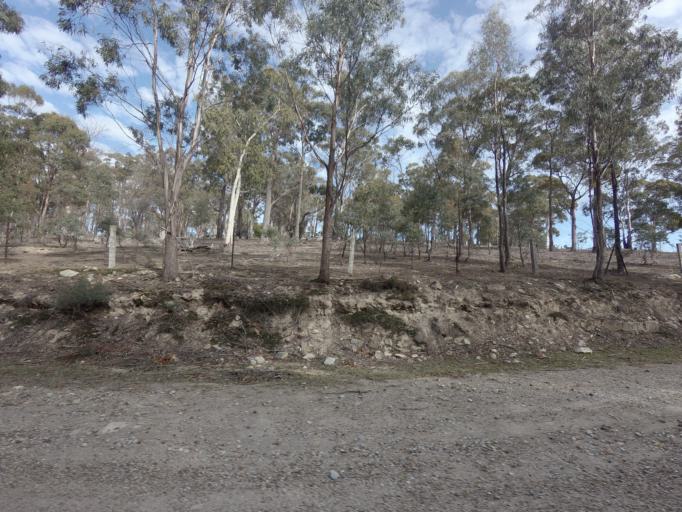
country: AU
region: Tasmania
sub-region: Sorell
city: Sorell
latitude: -42.5658
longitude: 147.4716
